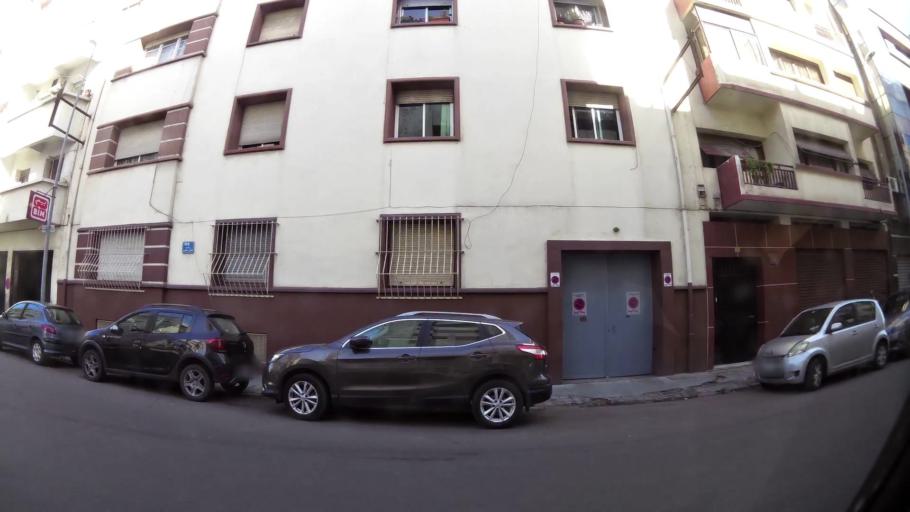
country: MA
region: Grand Casablanca
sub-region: Casablanca
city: Casablanca
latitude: 33.5927
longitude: -7.5904
